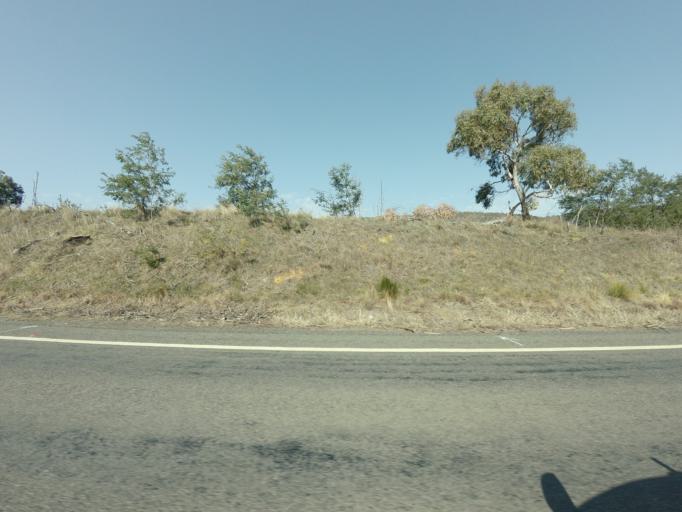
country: AU
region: Tasmania
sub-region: Northern Midlands
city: Evandale
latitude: -41.8117
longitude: 147.6177
